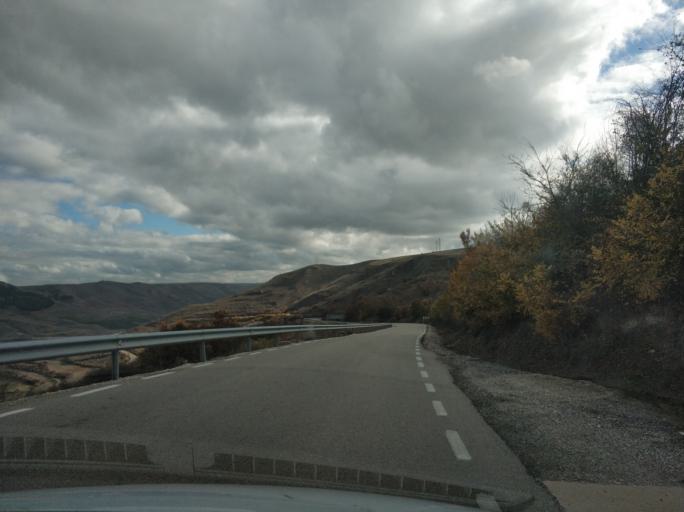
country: ES
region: Castille and Leon
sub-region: Provincia de Soria
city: Medinaceli
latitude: 41.1669
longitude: -2.4359
